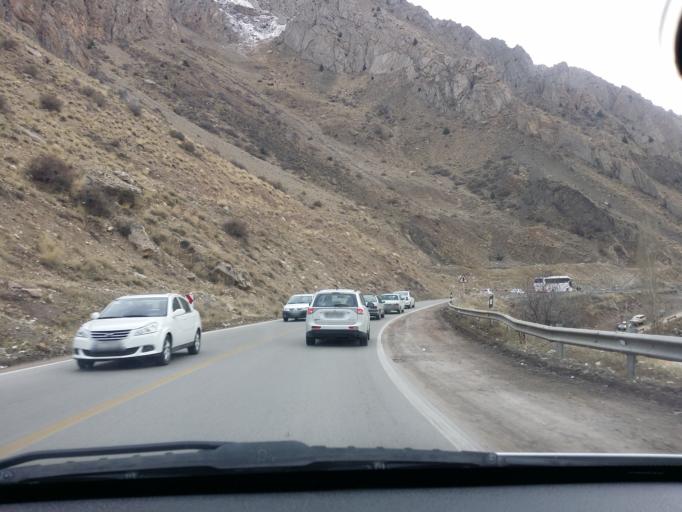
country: IR
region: Tehran
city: Tajrish
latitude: 36.0700
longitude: 51.3099
